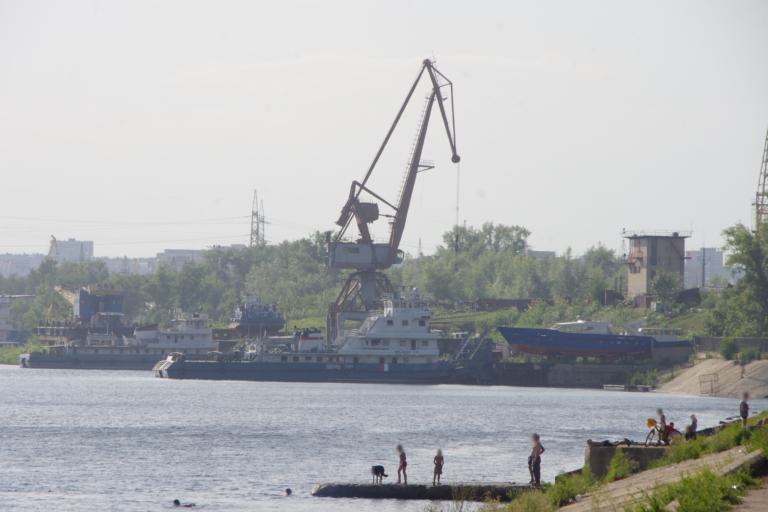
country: RU
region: Samara
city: Zhigulevsk
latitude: 53.4630
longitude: 49.5332
